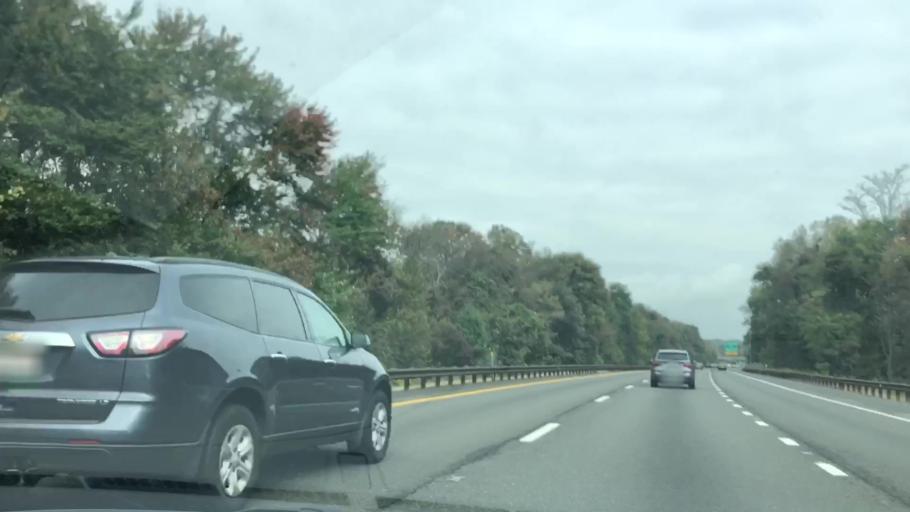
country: US
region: New Jersey
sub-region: Bergen County
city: Ho-Ho-Kus
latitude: 40.9918
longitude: -74.0729
